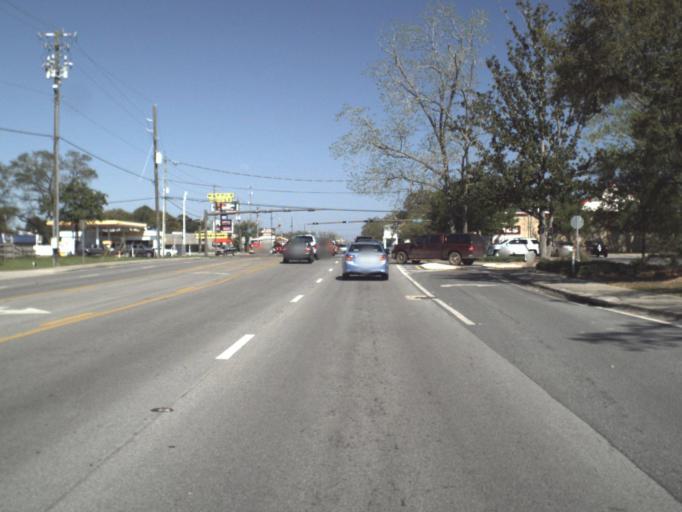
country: US
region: Florida
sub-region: Okaloosa County
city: Wright
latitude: 30.4495
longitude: -86.6402
